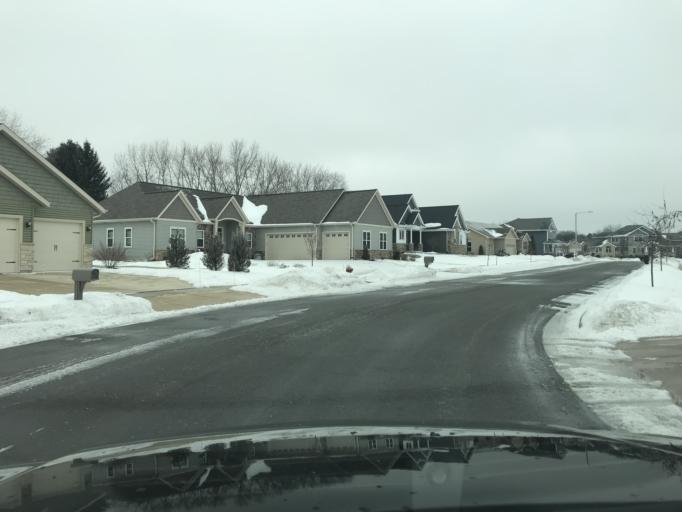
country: US
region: Wisconsin
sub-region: Dane County
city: Cottage Grove
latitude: 43.0944
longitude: -89.2144
